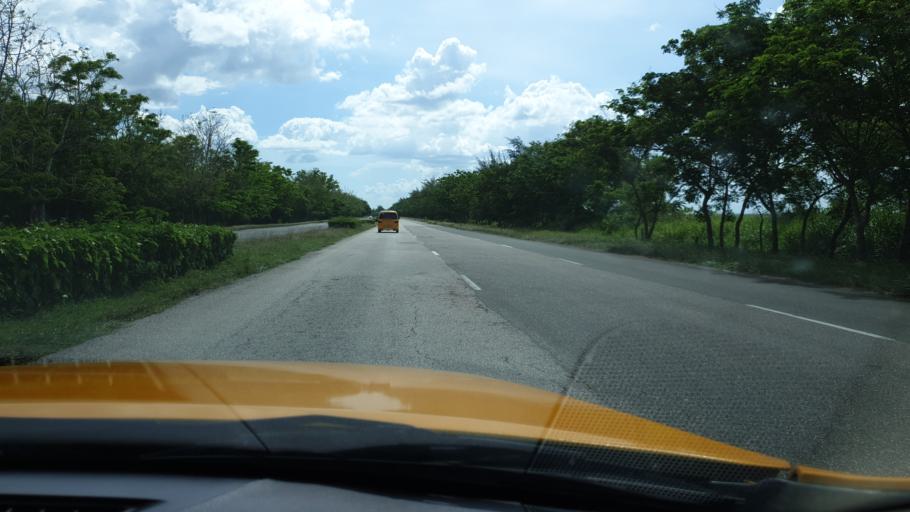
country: CU
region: Cienfuegos
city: Cruces
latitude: 22.4554
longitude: -80.3153
